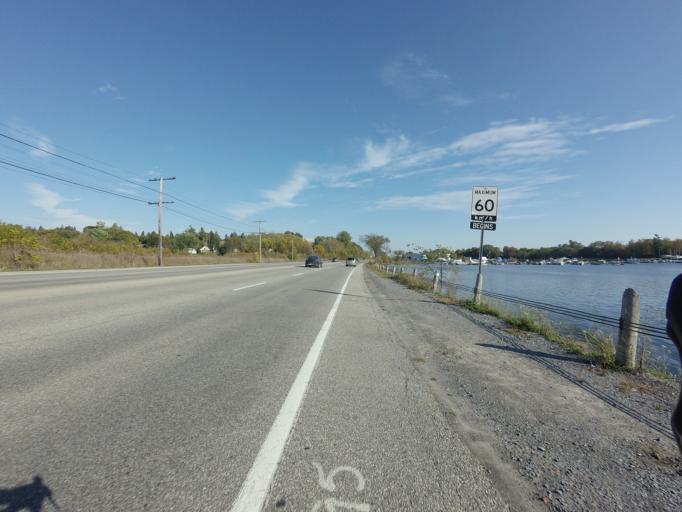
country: CA
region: Ontario
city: Kingston
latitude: 44.2420
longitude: -76.6045
